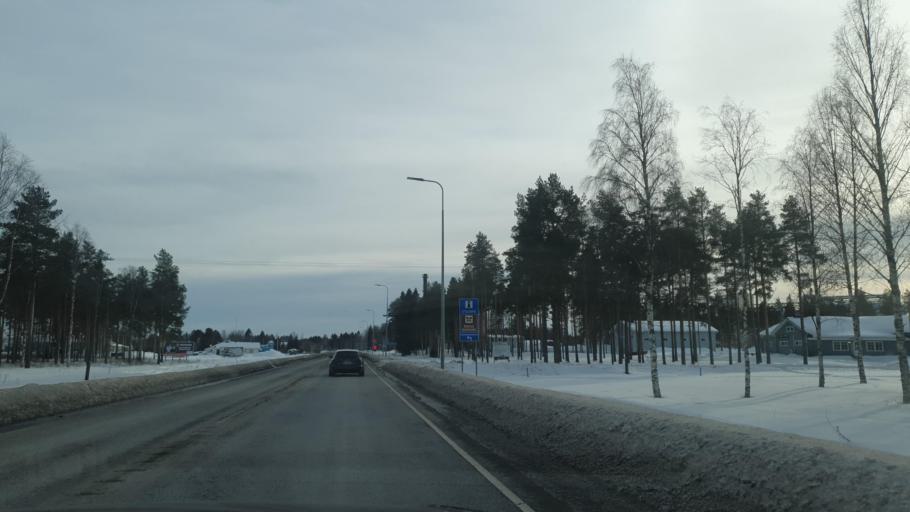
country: FI
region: Northern Ostrobothnia
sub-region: Oulunkaari
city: Utajaervi
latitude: 64.7658
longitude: 26.4081
